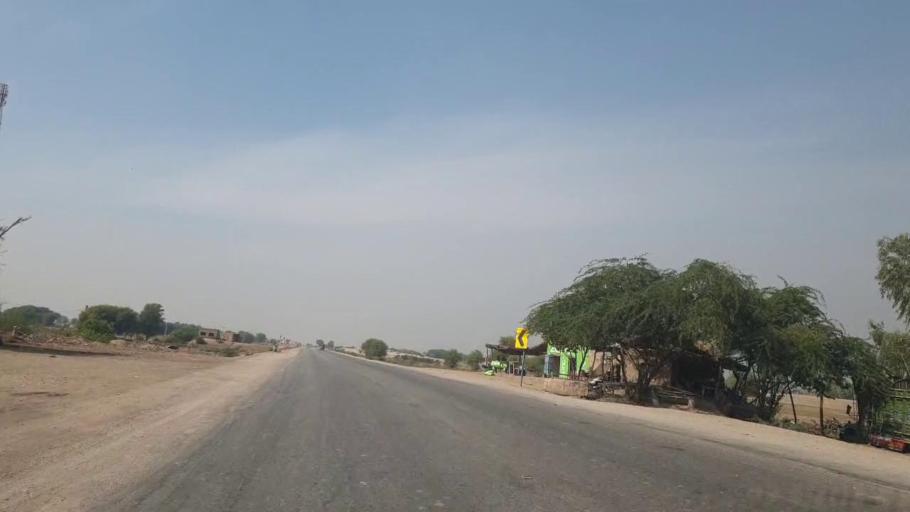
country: PK
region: Sindh
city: Sann
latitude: 25.9857
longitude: 68.1820
